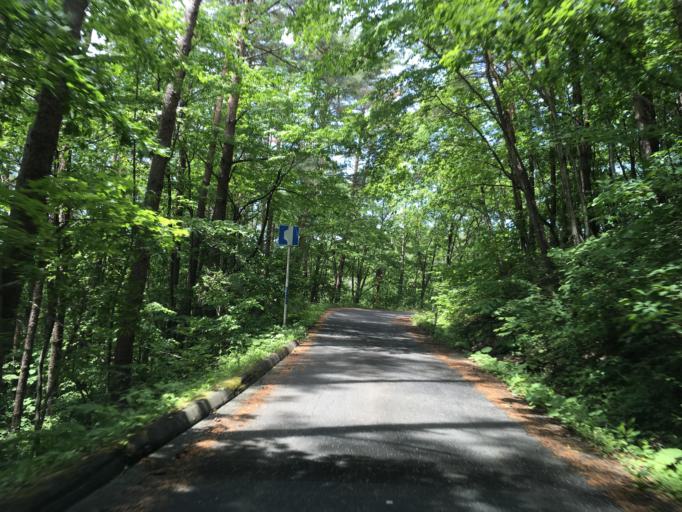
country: JP
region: Iwate
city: Mizusawa
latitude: 39.1262
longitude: 141.2905
